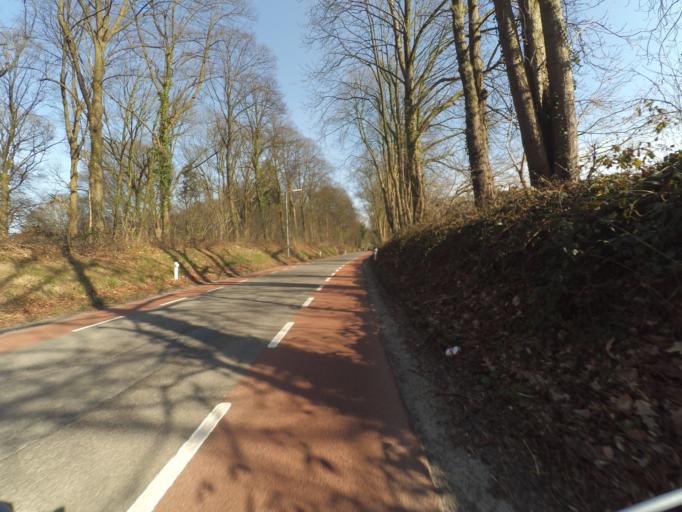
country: NL
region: Gelderland
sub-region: Gemeente Groesbeek
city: Berg en Dal
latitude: 51.8175
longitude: 5.9272
